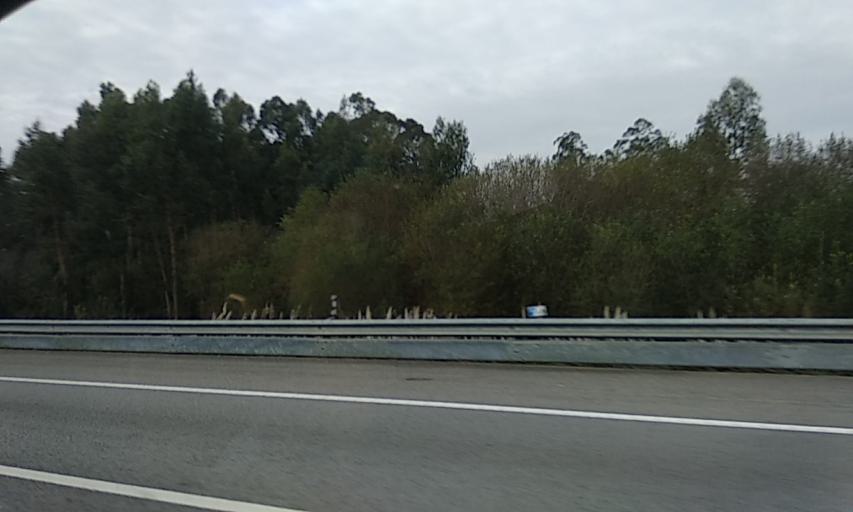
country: PT
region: Porto
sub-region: Trofa
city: Sao Romao do Coronado
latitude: 41.2685
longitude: -8.5613
